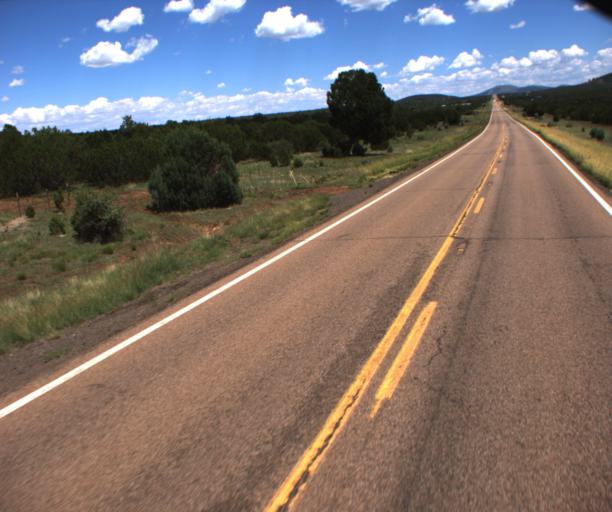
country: US
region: Arizona
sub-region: Navajo County
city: Pinetop-Lakeside
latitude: 34.2767
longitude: -109.7904
